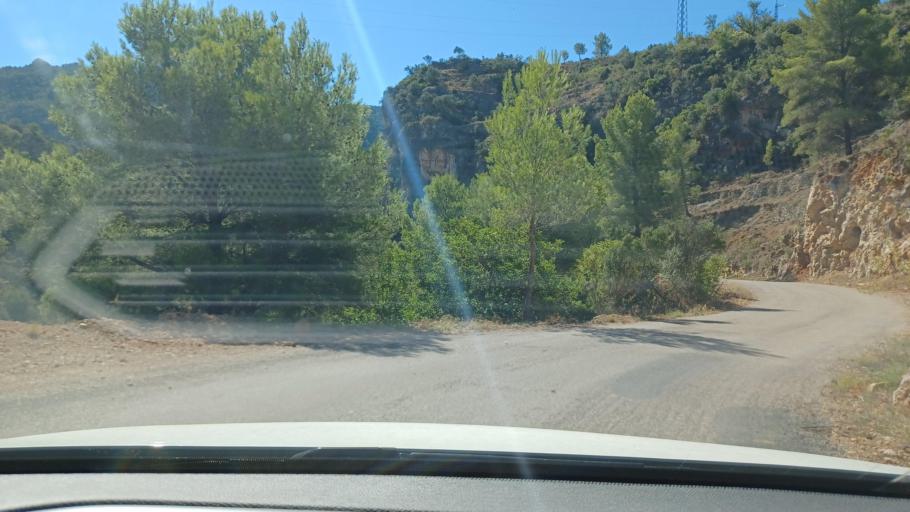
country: ES
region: Catalonia
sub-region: Provincia de Tarragona
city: Benifallet
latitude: 40.9522
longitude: 0.5101
